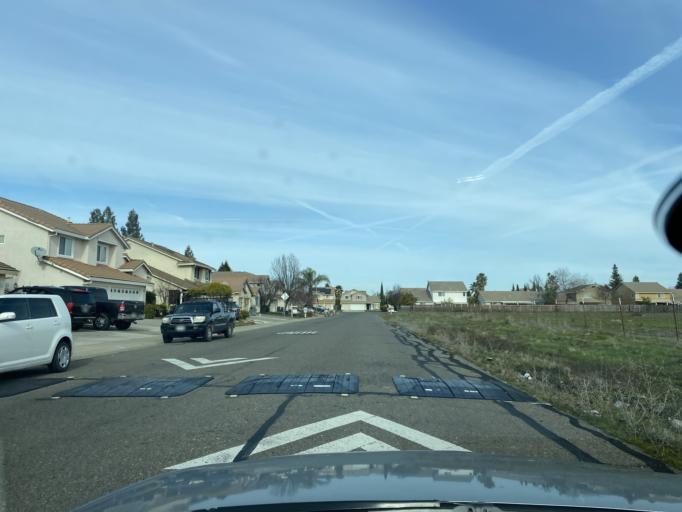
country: US
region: California
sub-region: Sacramento County
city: Elk Grove
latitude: 38.4397
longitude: -121.3839
